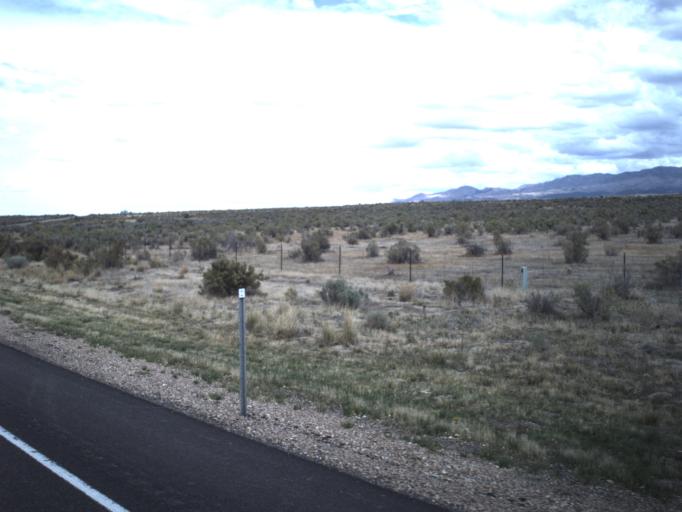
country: US
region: Utah
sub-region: Millard County
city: Fillmore
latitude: 39.1572
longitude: -112.4095
